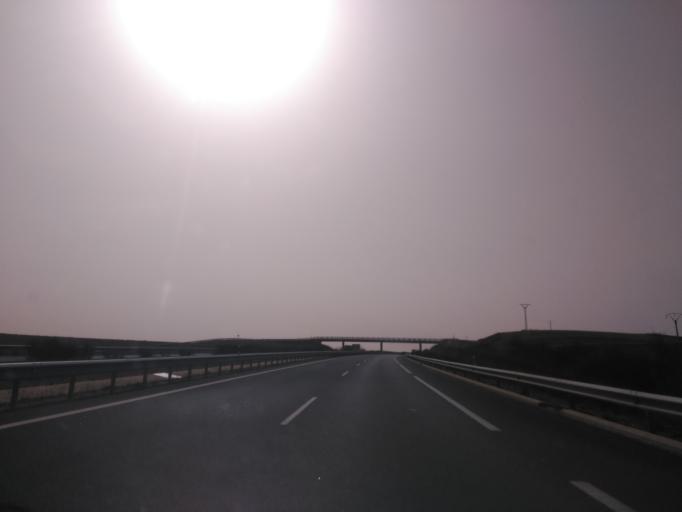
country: ES
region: Castille and Leon
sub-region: Provincia de Palencia
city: Marcilla de Campos
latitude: 42.3521
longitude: -4.3887
